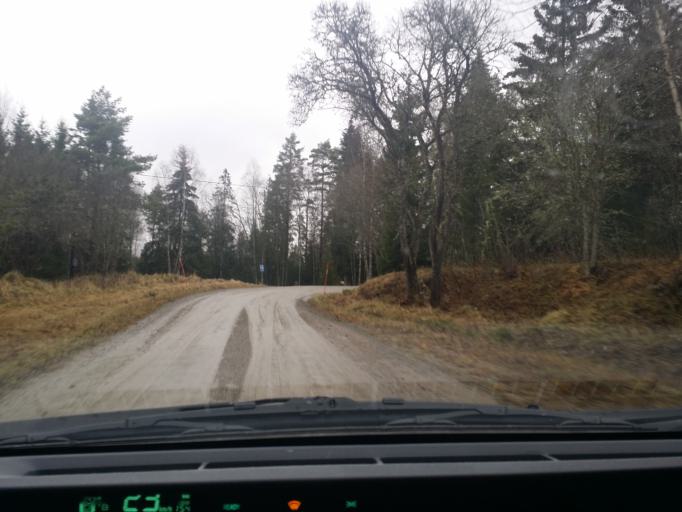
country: SE
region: Vaestmanland
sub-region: Vasteras
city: Skultuna
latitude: 59.7757
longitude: 16.3315
